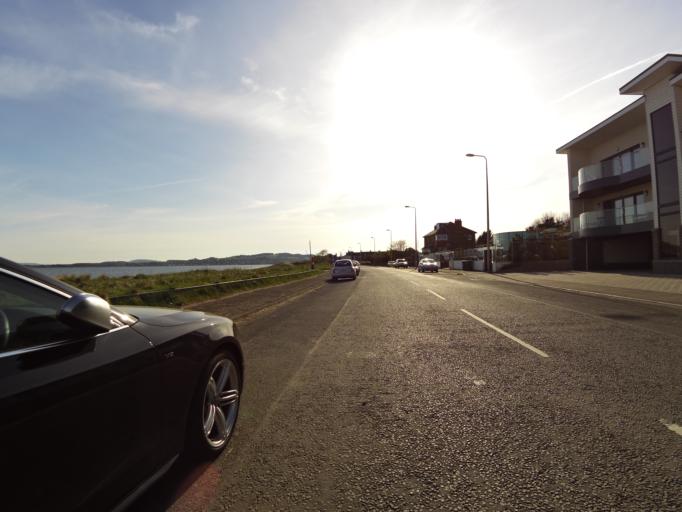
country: GB
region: Scotland
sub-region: Fife
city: Tayport
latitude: 56.4676
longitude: -2.8574
